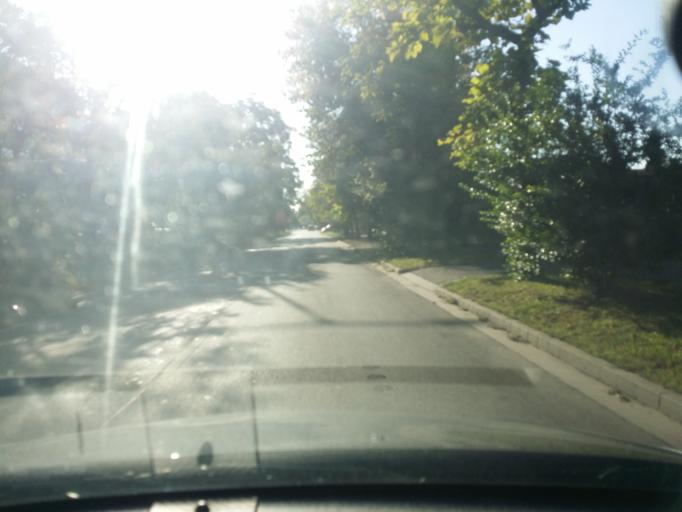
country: HU
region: Budapest
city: Budapest XV. keruelet
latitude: 47.5787
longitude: 19.1036
